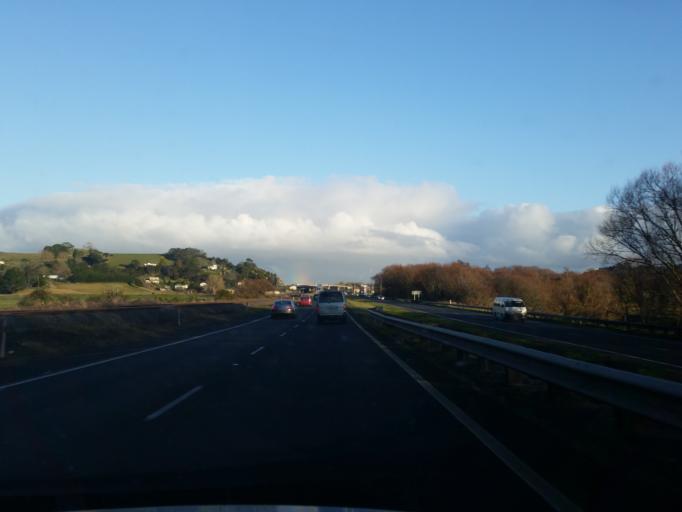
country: NZ
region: Auckland
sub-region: Auckland
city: Pukekohe East
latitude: -37.2704
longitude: 175.0458
